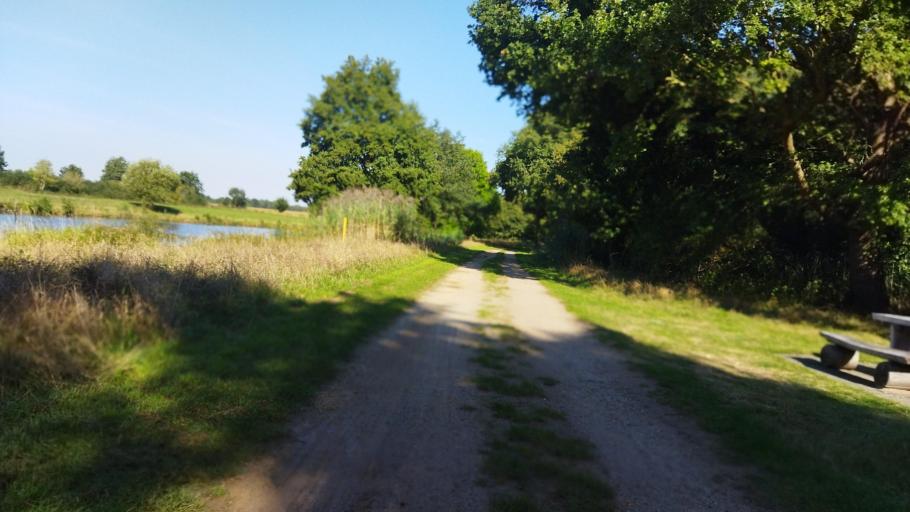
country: DE
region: Lower Saxony
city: Haren
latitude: 52.7658
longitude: 7.2547
